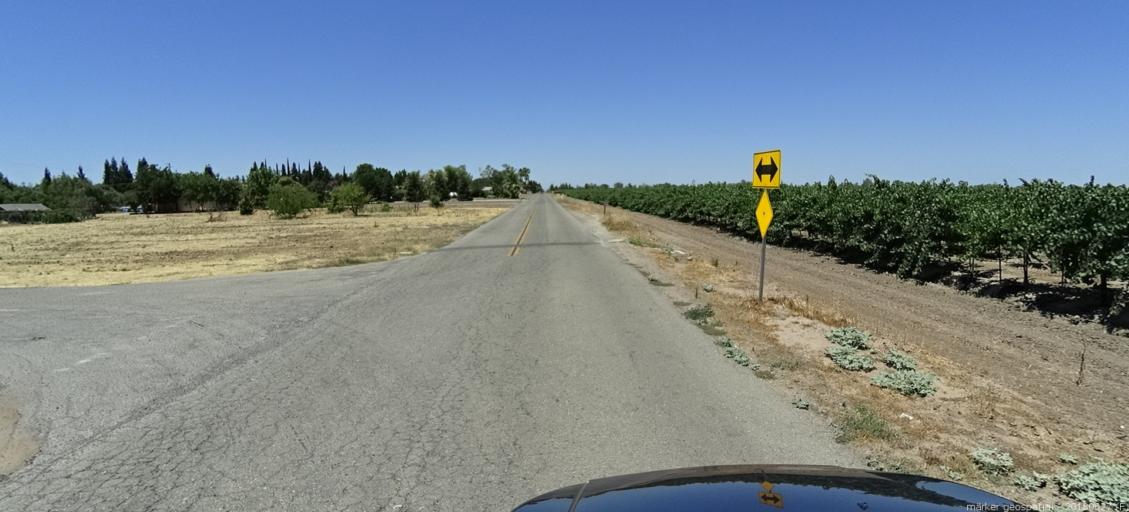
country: US
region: California
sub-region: Madera County
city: Bonadelle Ranchos-Madera Ranchos
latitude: 36.9375
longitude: -119.8821
